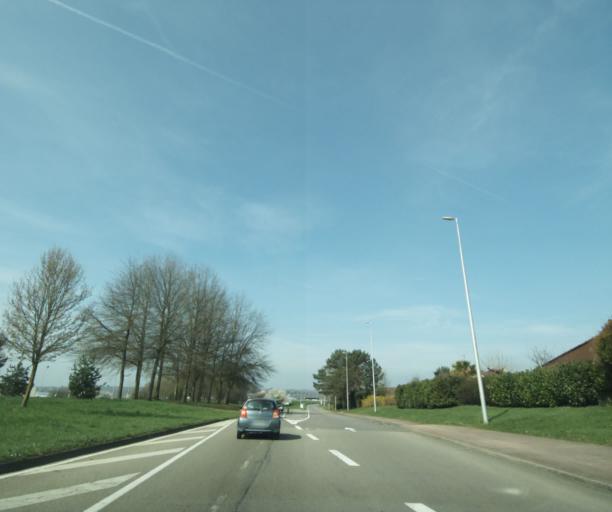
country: FR
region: Limousin
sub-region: Departement de la Haute-Vienne
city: Rilhac-Rancon
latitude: 45.8815
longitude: 1.2940
